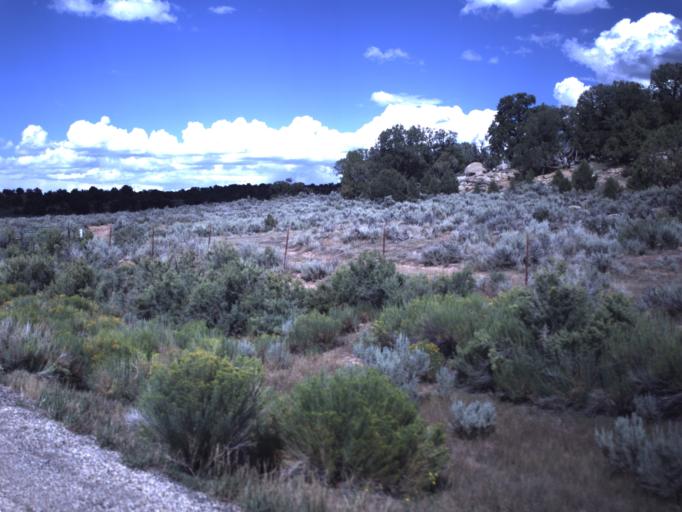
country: US
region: Utah
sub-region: Duchesne County
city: Duchesne
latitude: 40.2392
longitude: -110.7156
